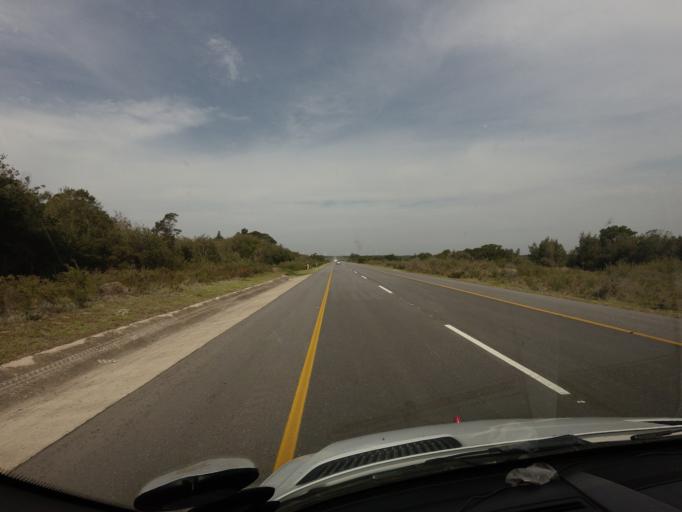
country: ZA
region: Eastern Cape
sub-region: Cacadu District Municipality
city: Kruisfontein
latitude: -33.9997
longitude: 24.7551
